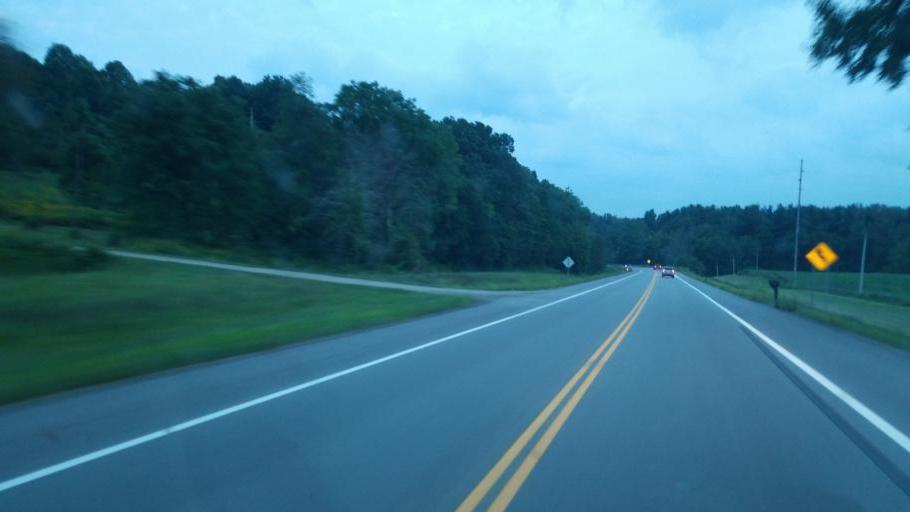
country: US
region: Ohio
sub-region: Sandusky County
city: Bellville
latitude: 40.6302
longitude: -82.5220
